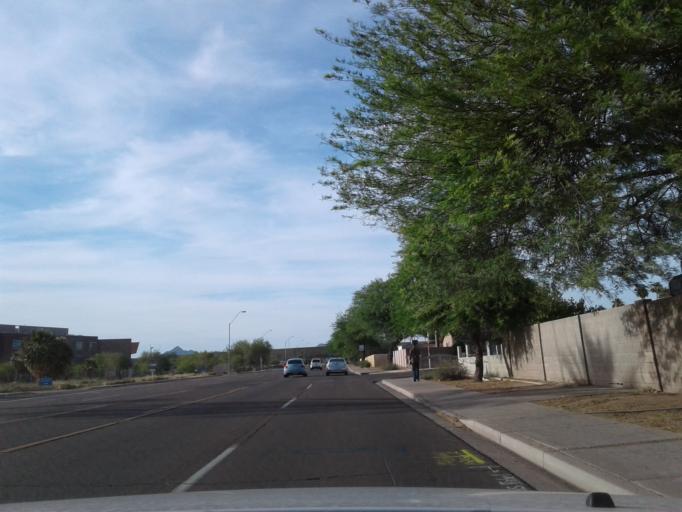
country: US
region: Arizona
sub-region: Maricopa County
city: Tempe Junction
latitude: 33.4543
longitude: -111.9952
